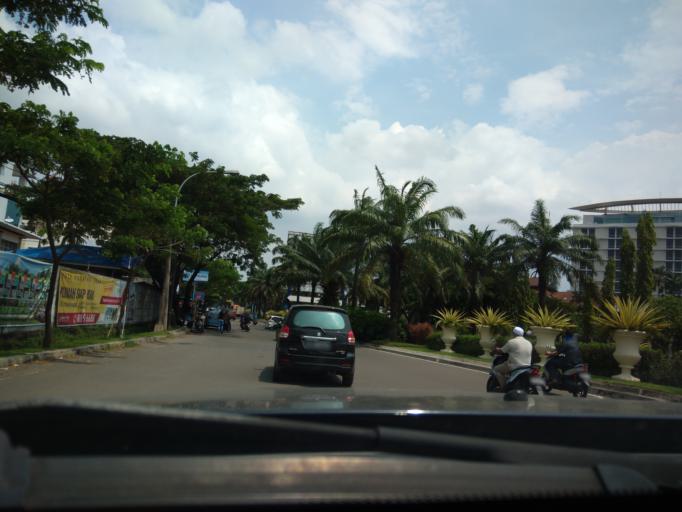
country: ID
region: West Java
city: Bekasi
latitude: -6.1835
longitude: 106.9773
